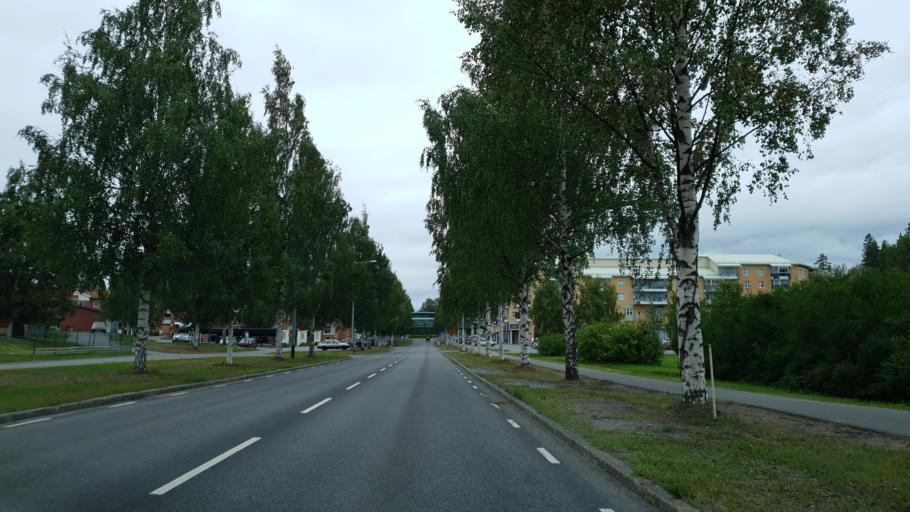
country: SE
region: Vaesterbotten
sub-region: Skelleftea Kommun
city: Skelleftea
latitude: 64.7591
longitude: 20.9567
